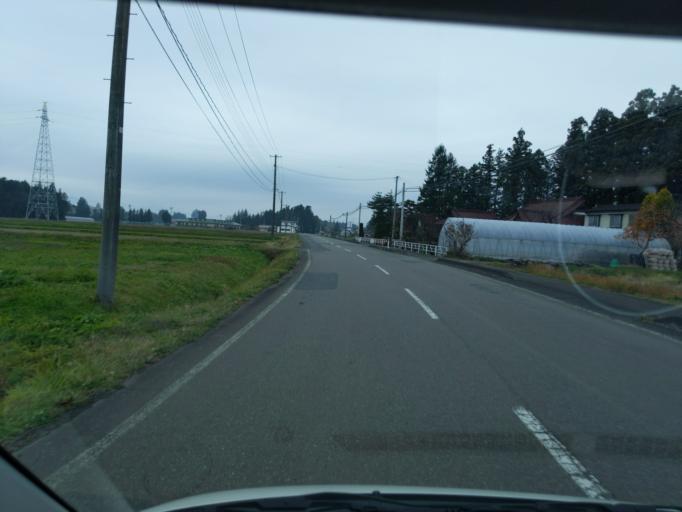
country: JP
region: Iwate
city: Mizusawa
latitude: 39.0986
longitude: 141.0879
